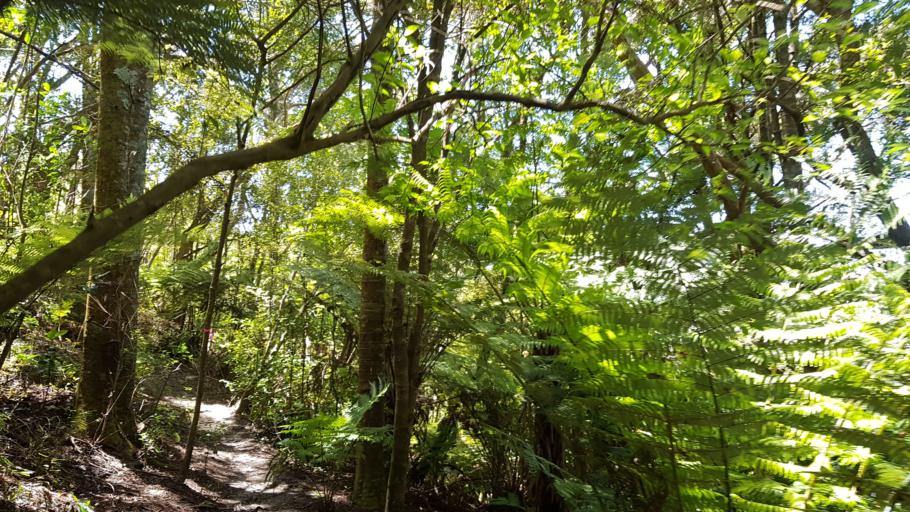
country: NZ
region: Auckland
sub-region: Auckland
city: North Shore
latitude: -36.8226
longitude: 174.7176
